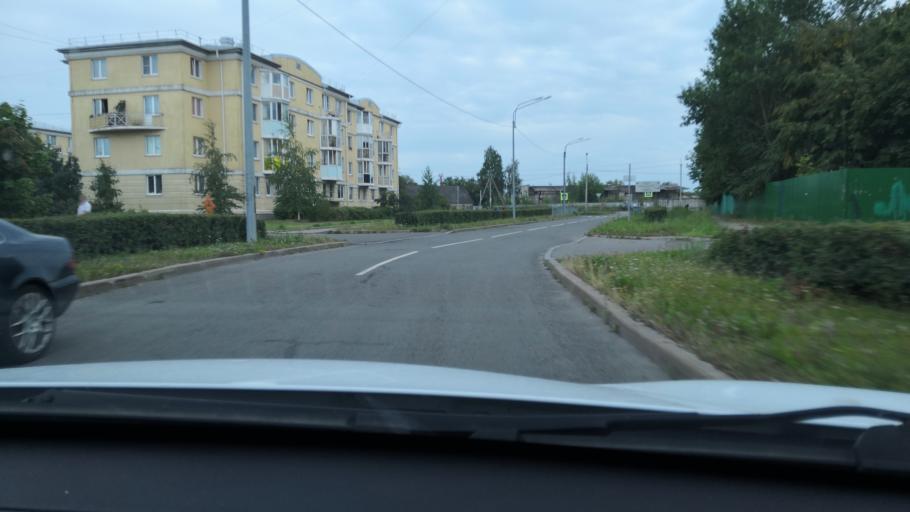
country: RU
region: St.-Petersburg
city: Pushkin
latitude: 59.7015
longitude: 30.3884
